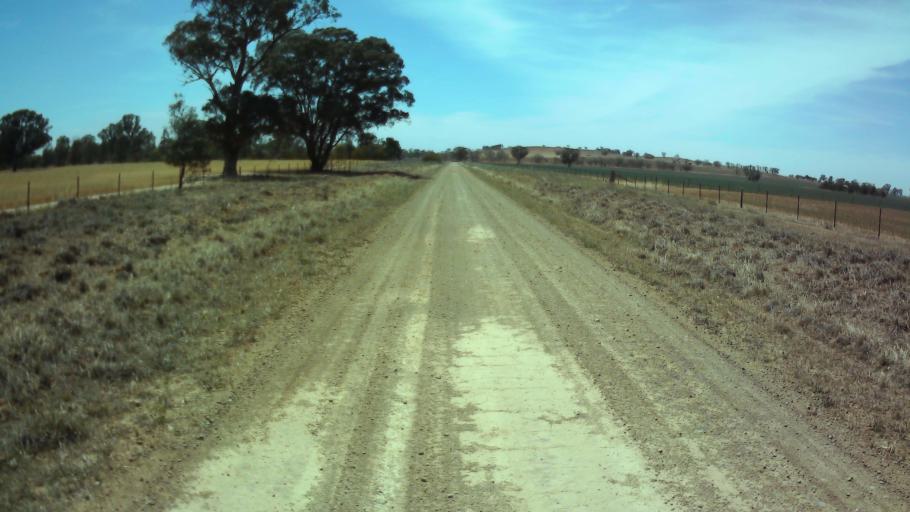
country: AU
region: New South Wales
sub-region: Weddin
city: Grenfell
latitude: -33.9919
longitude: 148.1489
